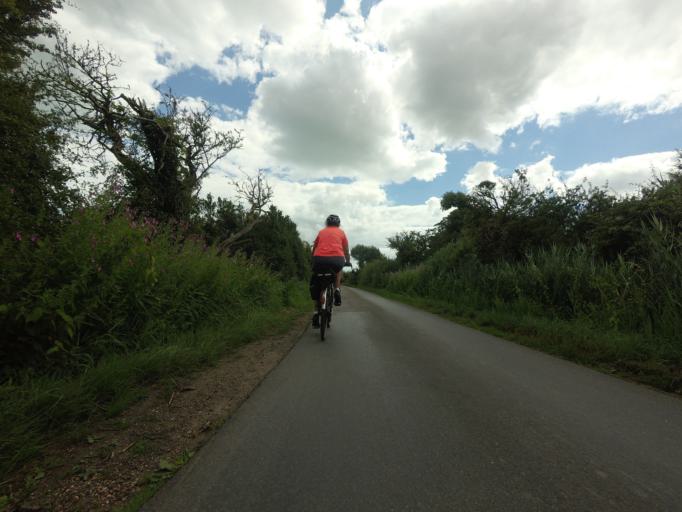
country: GB
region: England
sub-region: East Sussex
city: Pevensey
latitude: 50.8305
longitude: 0.3296
